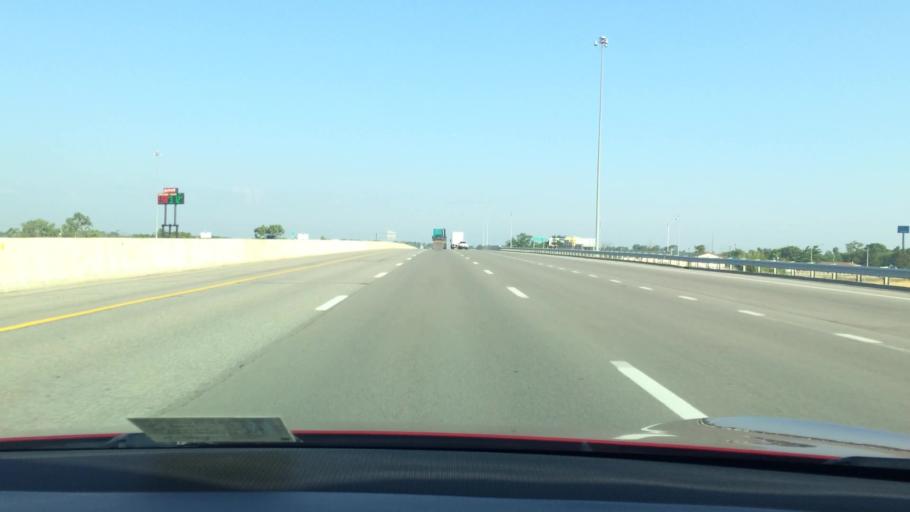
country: US
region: Ohio
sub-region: Wood County
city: Millbury
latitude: 41.5251
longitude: -83.4608
